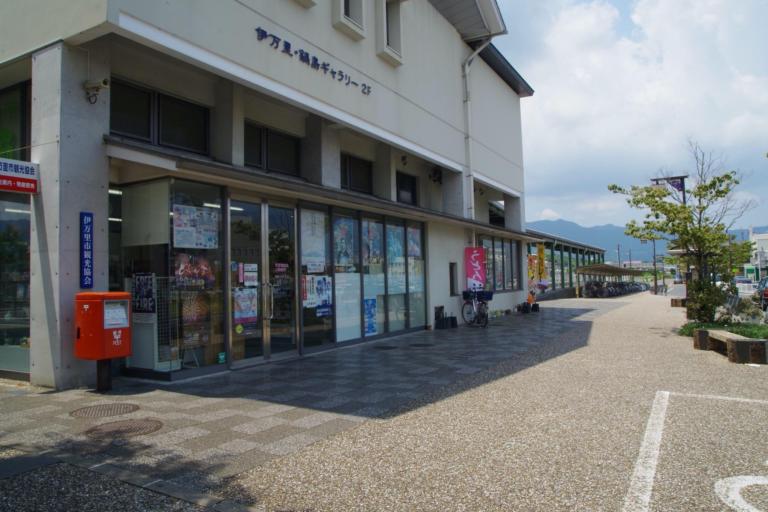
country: JP
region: Saga Prefecture
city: Imaricho-ko
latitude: 33.2720
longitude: 129.8764
